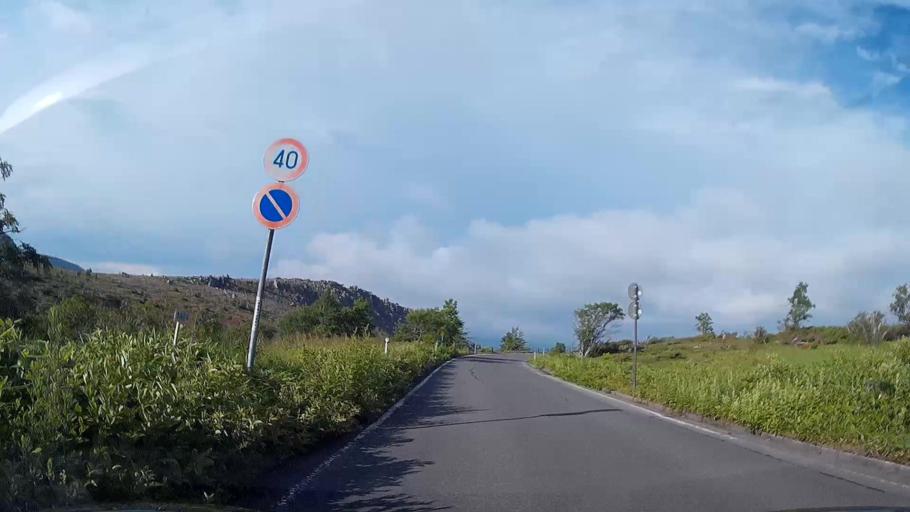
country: JP
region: Nagano
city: Nakano
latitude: 36.6353
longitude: 138.5420
